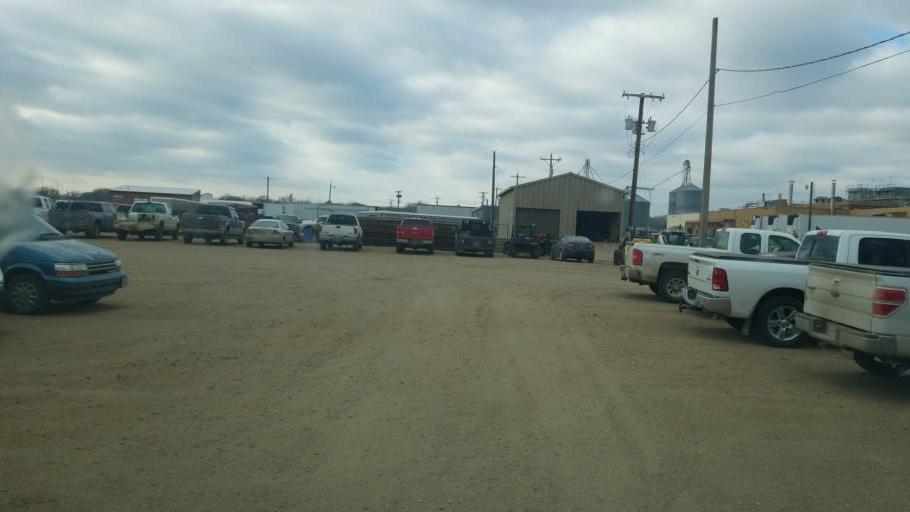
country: US
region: South Dakota
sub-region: Yankton County
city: Yankton
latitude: 42.8750
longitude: -97.3756
